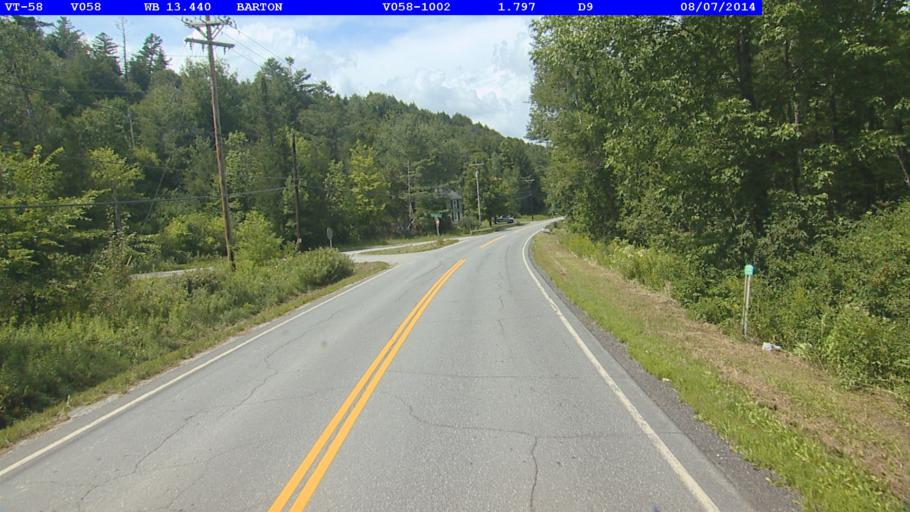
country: US
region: Vermont
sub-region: Orleans County
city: Newport
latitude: 44.8019
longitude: -72.1779
